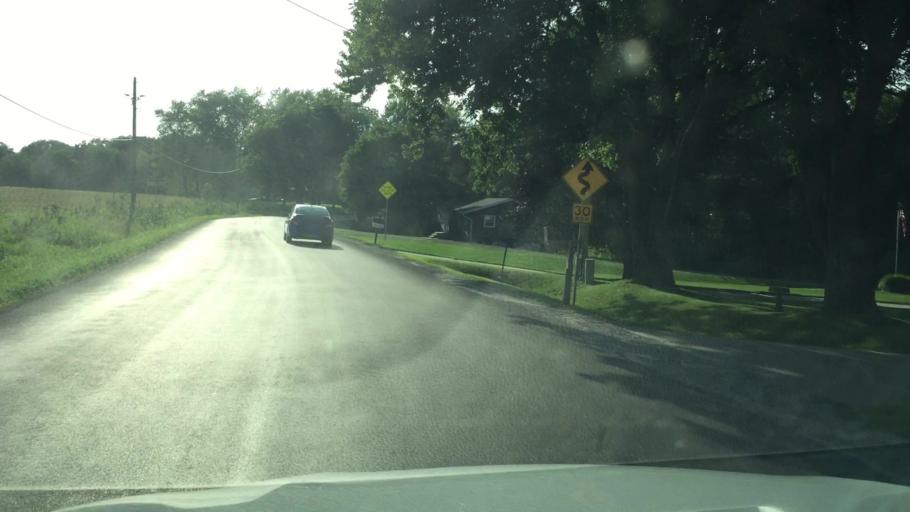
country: US
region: Iowa
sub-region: Linn County
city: Ely
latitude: 41.8275
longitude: -91.6236
